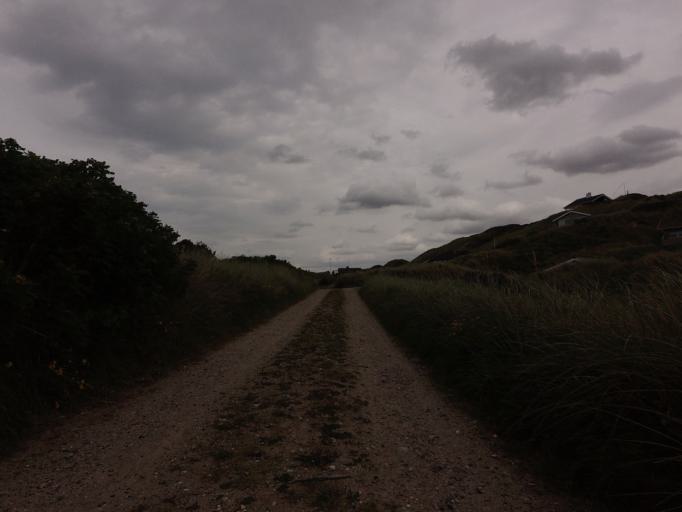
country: DK
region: North Denmark
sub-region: Jammerbugt Kommune
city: Pandrup
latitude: 57.3118
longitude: 9.6502
